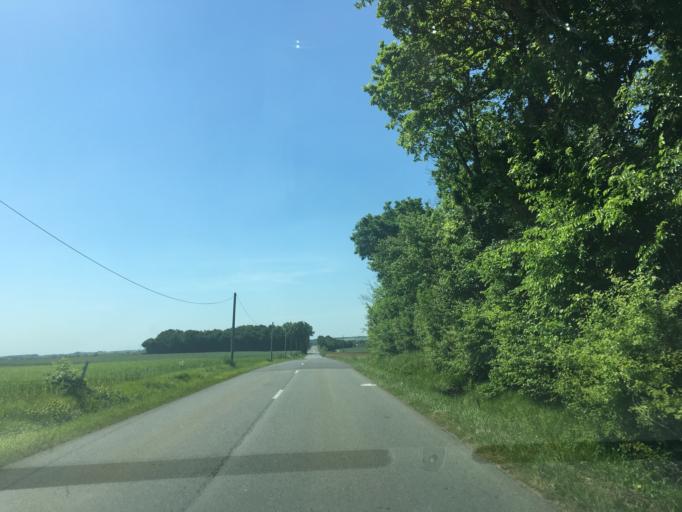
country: FR
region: Poitou-Charentes
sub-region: Departement des Deux-Sevres
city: Beauvoir-sur-Niort
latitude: 46.0770
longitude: -0.5215
